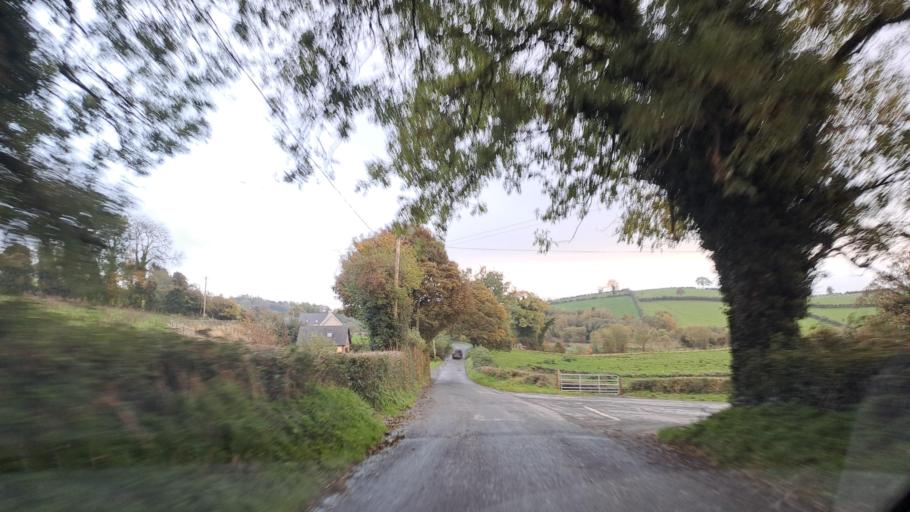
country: IE
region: Ulster
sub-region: County Monaghan
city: Carrickmacross
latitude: 53.9833
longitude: -6.6874
